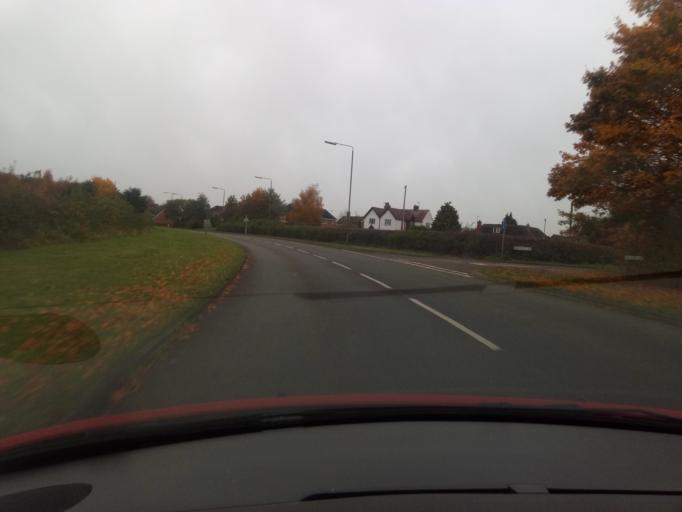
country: GB
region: England
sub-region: Derbyshire
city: Borrowash
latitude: 52.8741
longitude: -1.4240
